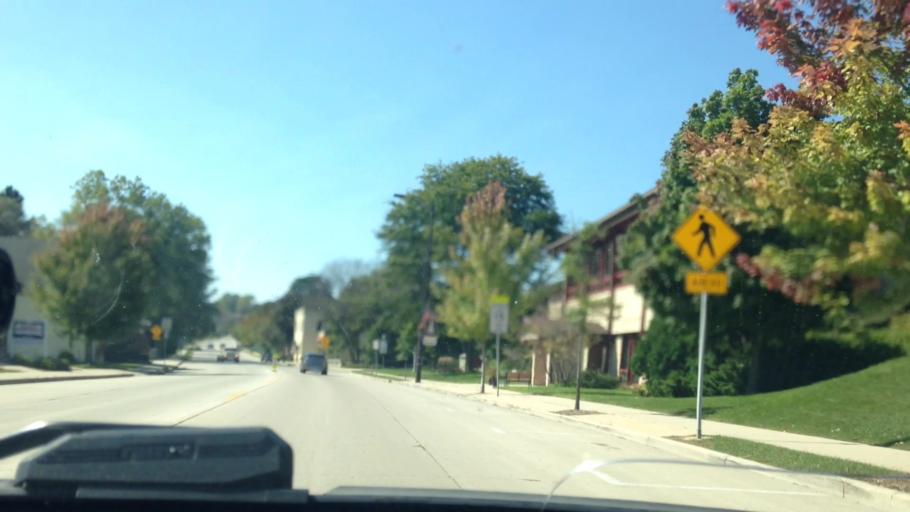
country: US
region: Wisconsin
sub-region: Ozaukee County
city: Port Washington
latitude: 43.3876
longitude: -87.8743
